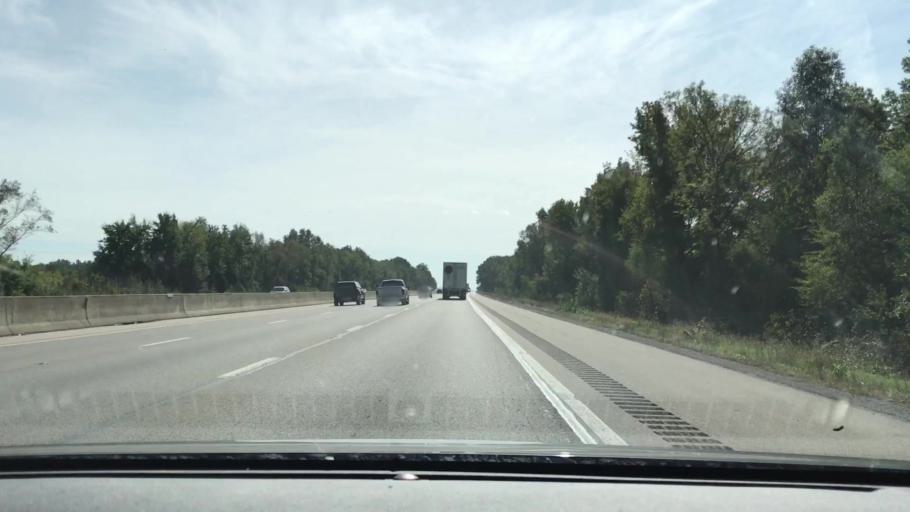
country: US
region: Kentucky
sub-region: Warren County
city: Plano
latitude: 36.8582
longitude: -86.4551
